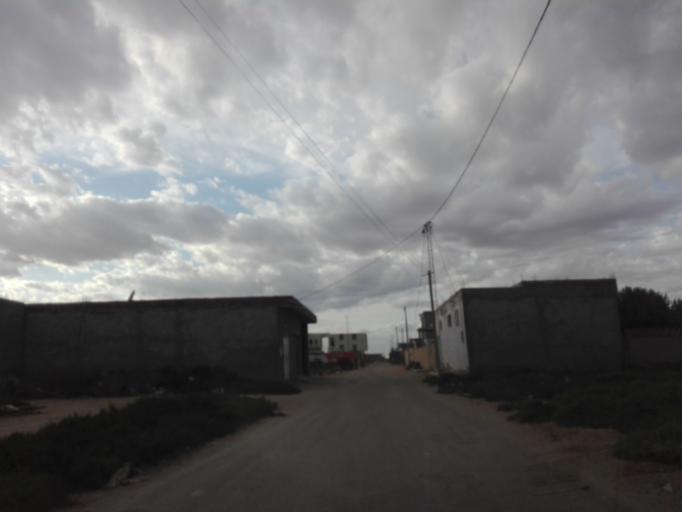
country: TN
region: Safaqis
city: Al Qarmadah
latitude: 34.8060
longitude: 10.8615
